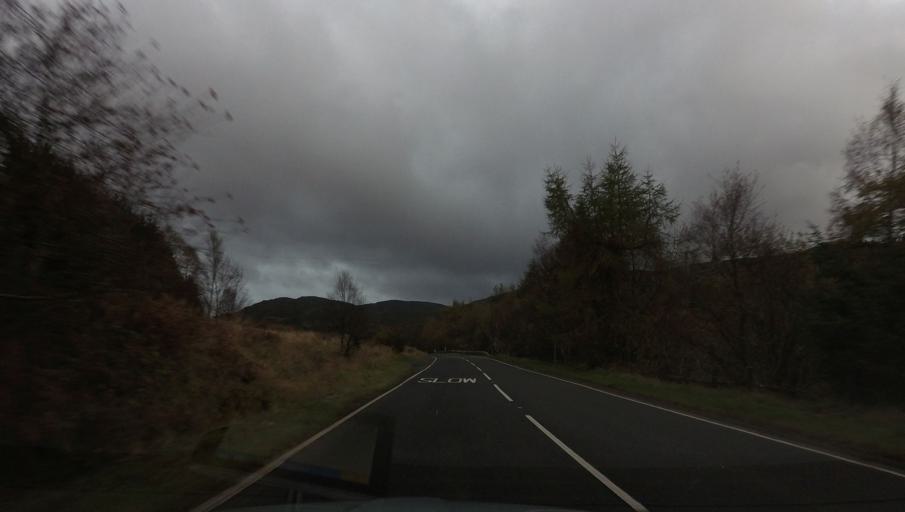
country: GB
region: Scotland
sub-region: Stirling
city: Callander
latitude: 56.4246
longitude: -4.3386
